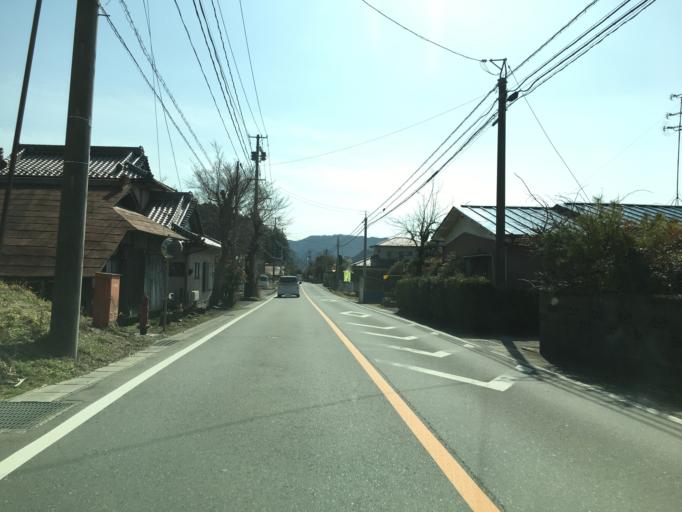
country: JP
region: Ibaraki
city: Daigo
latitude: 36.8851
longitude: 140.4204
